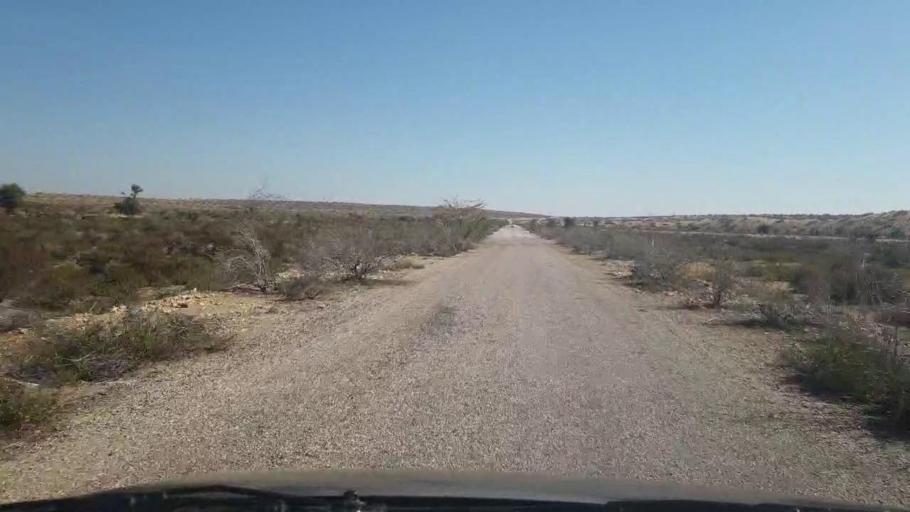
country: PK
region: Sindh
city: Bozdar
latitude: 27.0209
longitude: 68.7222
